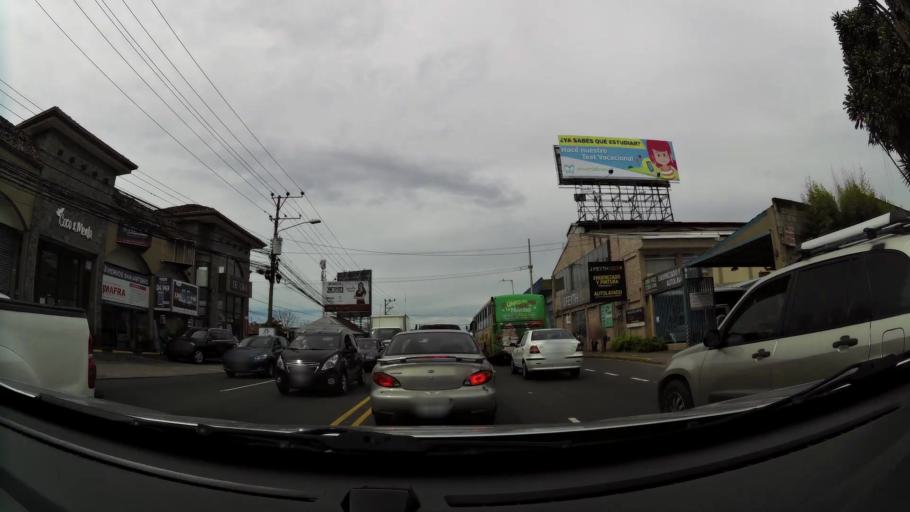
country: CR
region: San Jose
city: San Pedro
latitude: 9.9304
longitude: -84.0449
